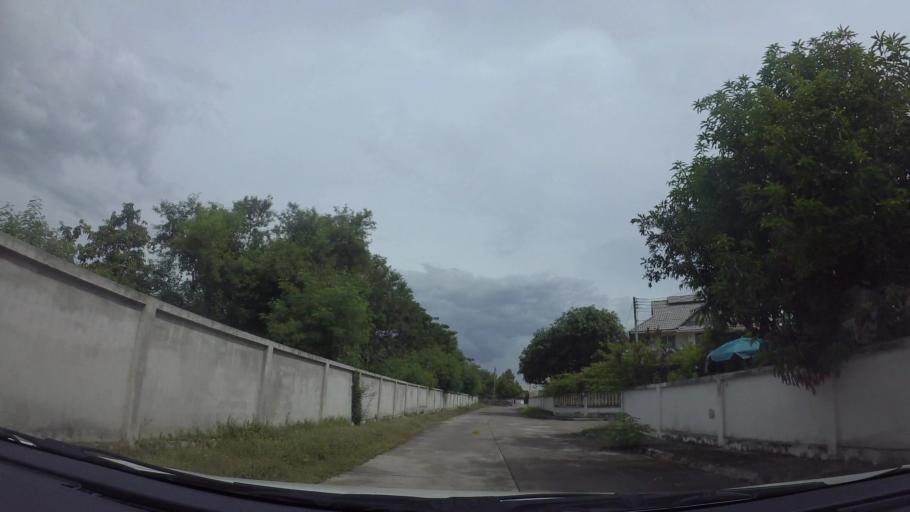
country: TH
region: Chiang Mai
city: Chiang Mai
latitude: 18.7501
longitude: 98.9798
